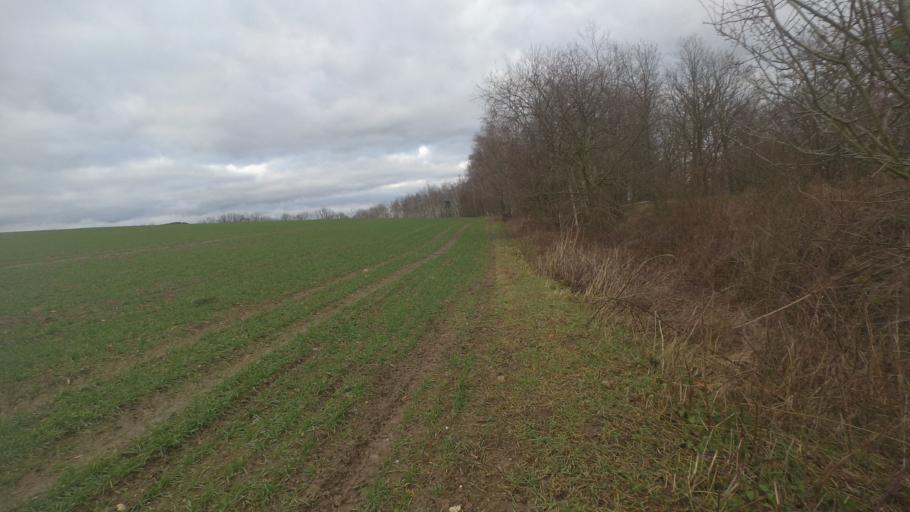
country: DE
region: Thuringia
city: Orlamunde
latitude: 50.7626
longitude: 11.5078
